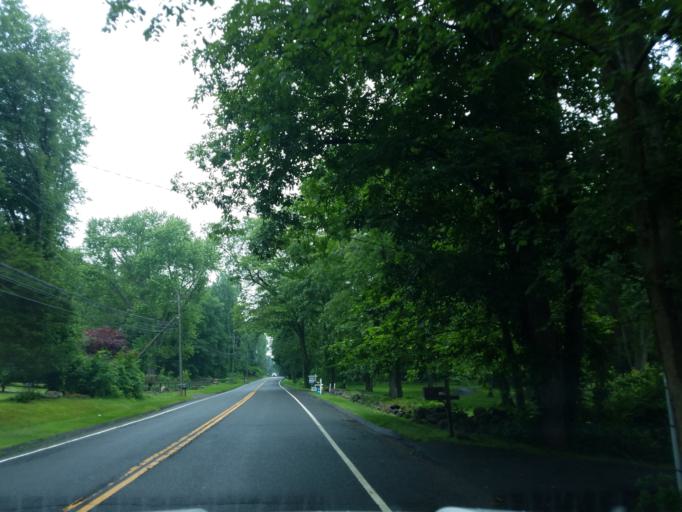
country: US
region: Connecticut
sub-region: Fairfield County
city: Georgetown
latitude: 41.2344
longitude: -73.4054
